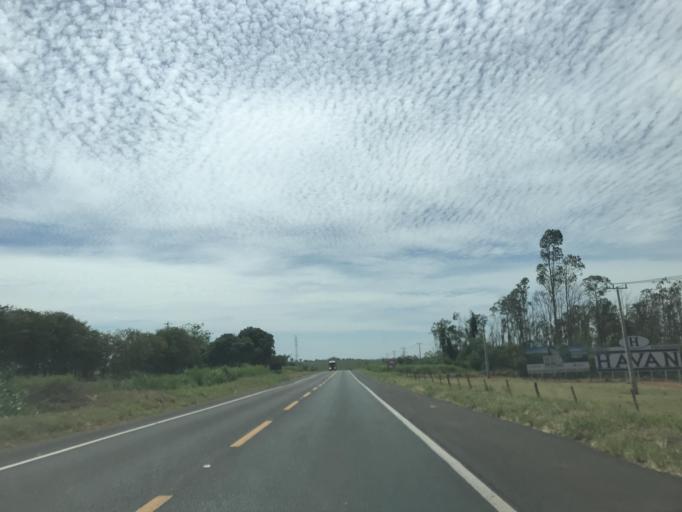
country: BR
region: Parana
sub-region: Paranavai
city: Paranavai
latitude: -23.0147
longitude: -52.5215
